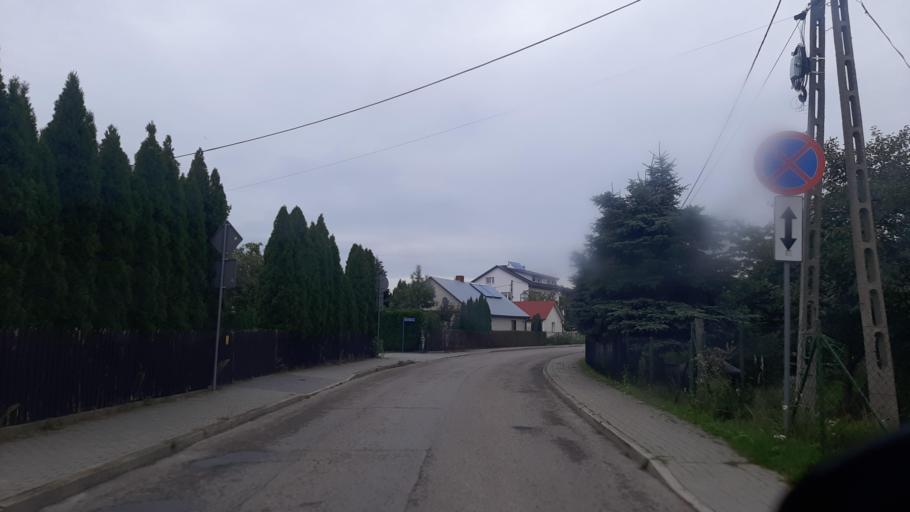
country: PL
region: Lublin Voivodeship
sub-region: Powiat lubartowski
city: Firlej
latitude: 51.5590
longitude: 22.5067
